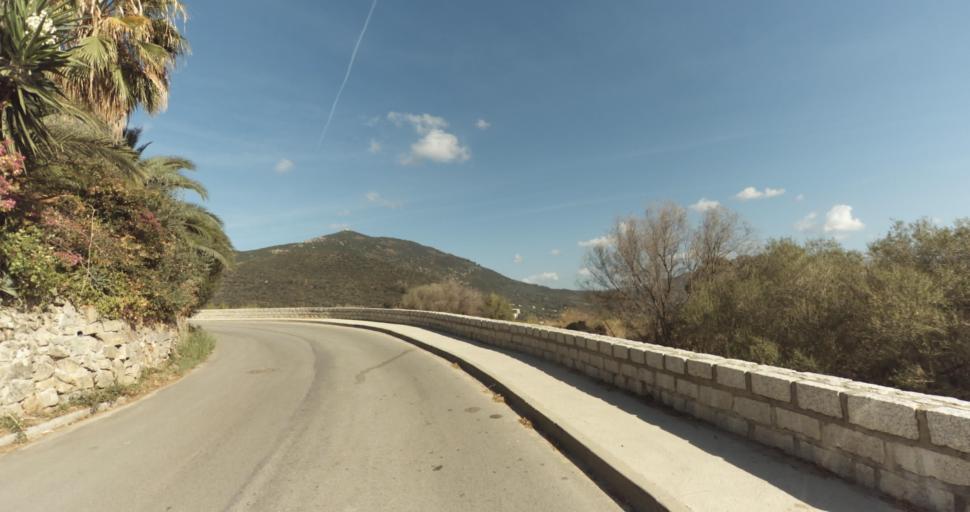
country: FR
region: Corsica
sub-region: Departement de la Corse-du-Sud
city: Ajaccio
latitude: 41.9258
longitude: 8.7182
